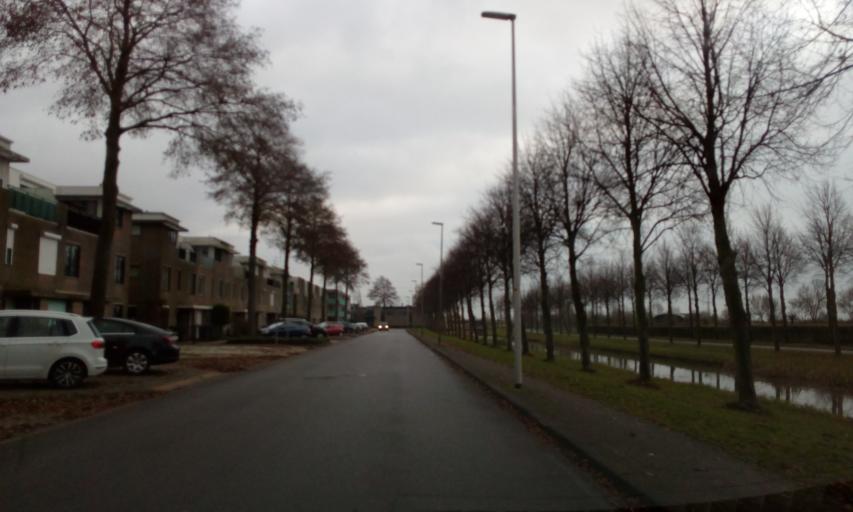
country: NL
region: South Holland
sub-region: Gemeente Zoetermeer
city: Zoetermeer
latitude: 52.0357
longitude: 4.4910
